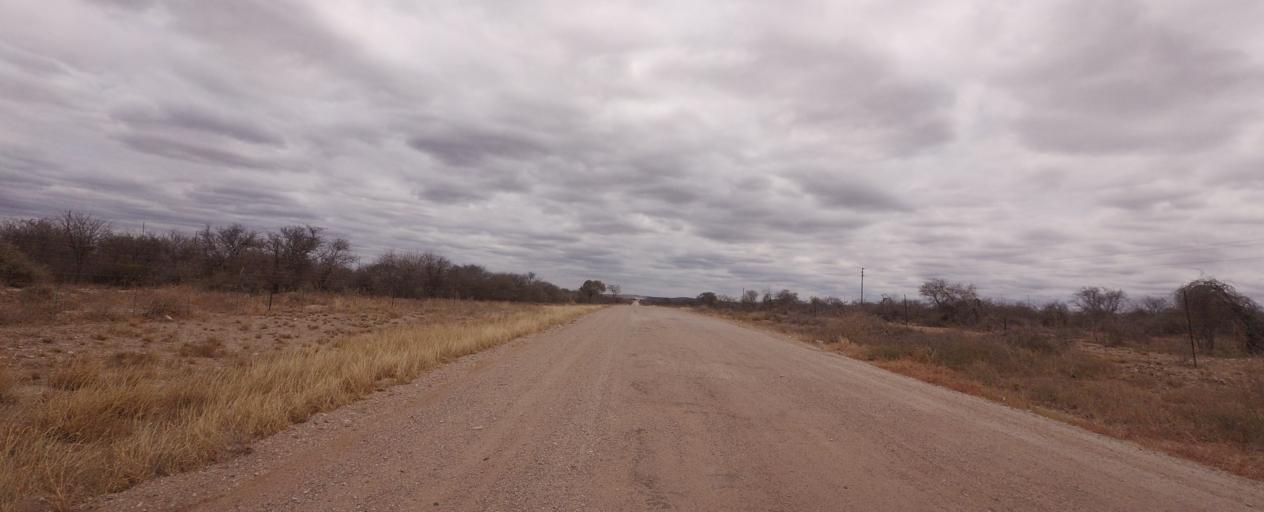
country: BW
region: Central
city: Mathathane
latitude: -22.7040
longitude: 28.6068
